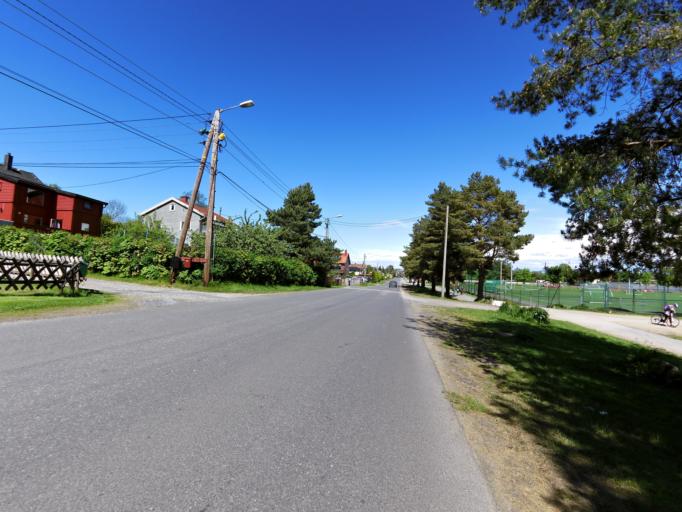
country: NO
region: Ostfold
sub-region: Fredrikstad
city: Fredrikstad
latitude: 59.2290
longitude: 10.9696
